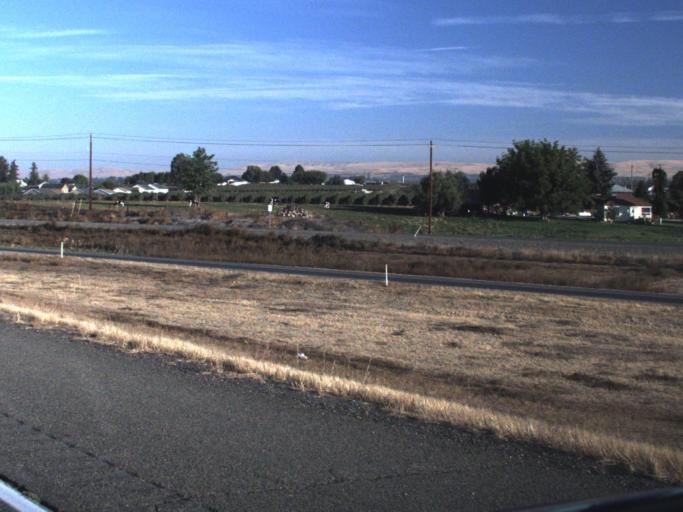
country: US
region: Washington
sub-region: Yakima County
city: Granger
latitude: 46.3467
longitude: -120.1788
